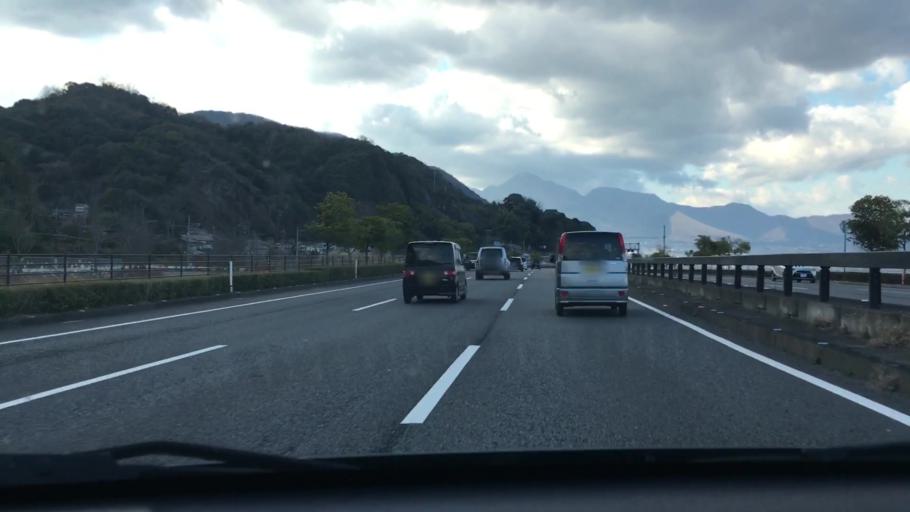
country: JP
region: Oita
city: Oita
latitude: 33.2521
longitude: 131.5681
